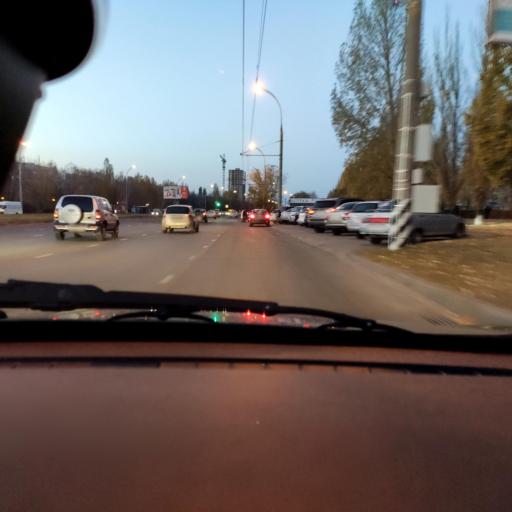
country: RU
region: Samara
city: Tol'yatti
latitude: 53.5201
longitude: 49.2957
